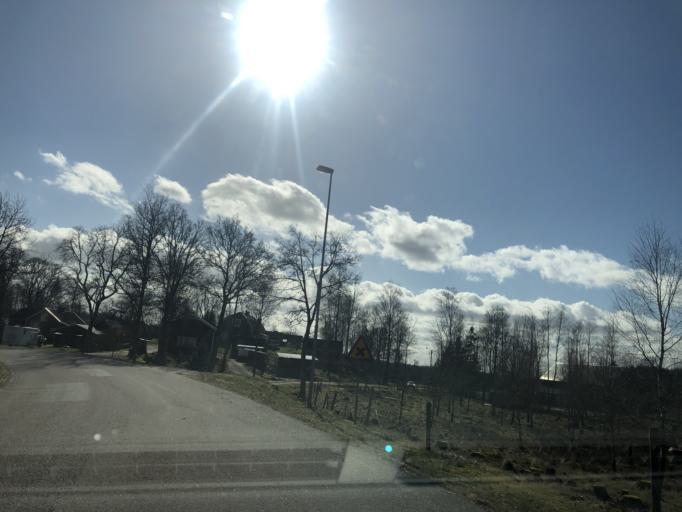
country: SE
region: Vaestra Goetaland
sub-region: Ulricehamns Kommun
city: Ulricehamn
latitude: 57.6884
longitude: 13.4177
